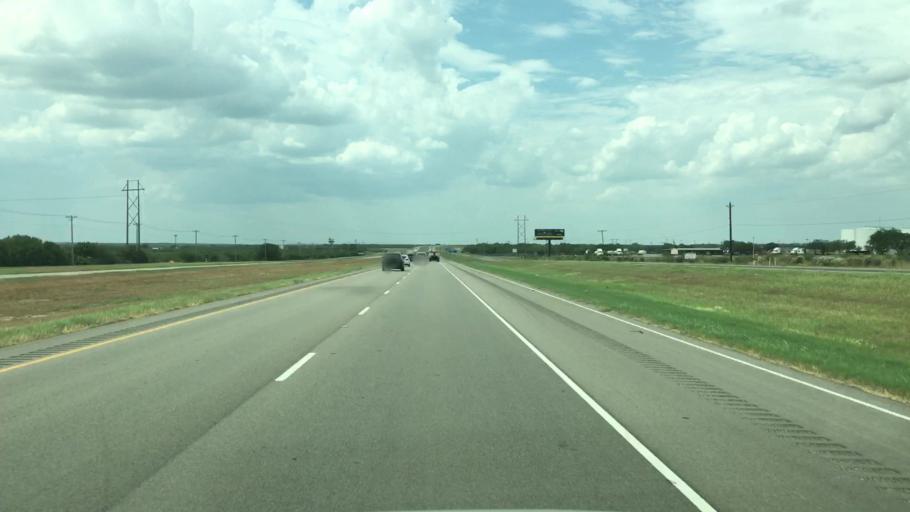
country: US
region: Texas
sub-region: Live Oak County
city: Three Rivers
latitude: 28.5109
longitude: -98.1687
